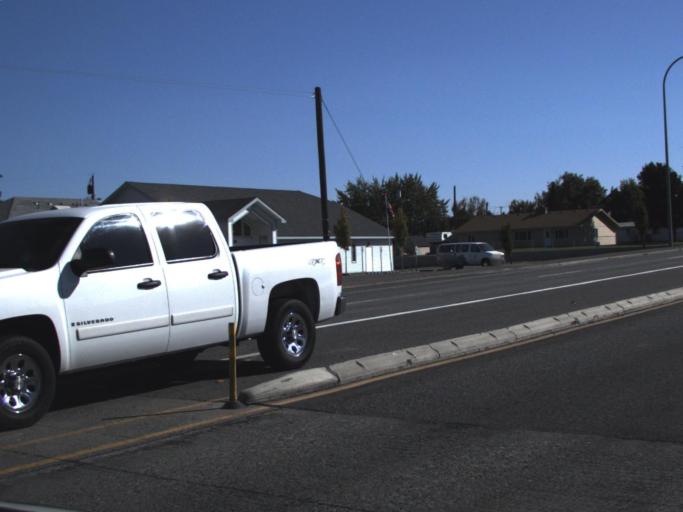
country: US
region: Washington
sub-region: Benton County
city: Kennewick
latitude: 46.2019
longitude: -119.1590
